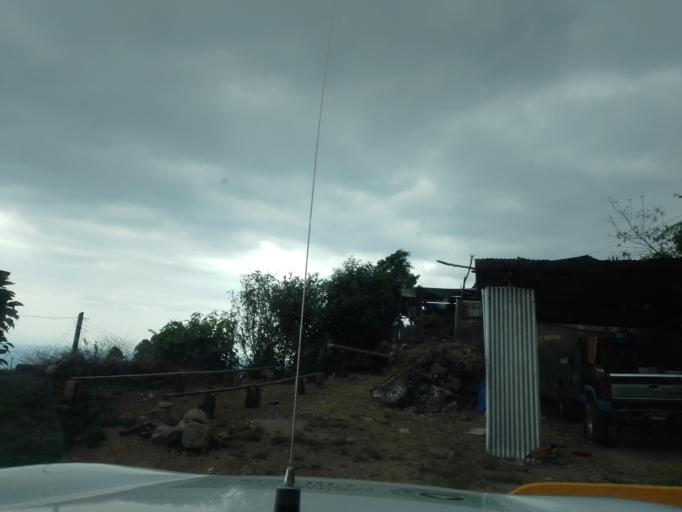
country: MX
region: Chiapas
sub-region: Union Juarez
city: Santo Domingo
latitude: 15.0679
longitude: -92.1137
